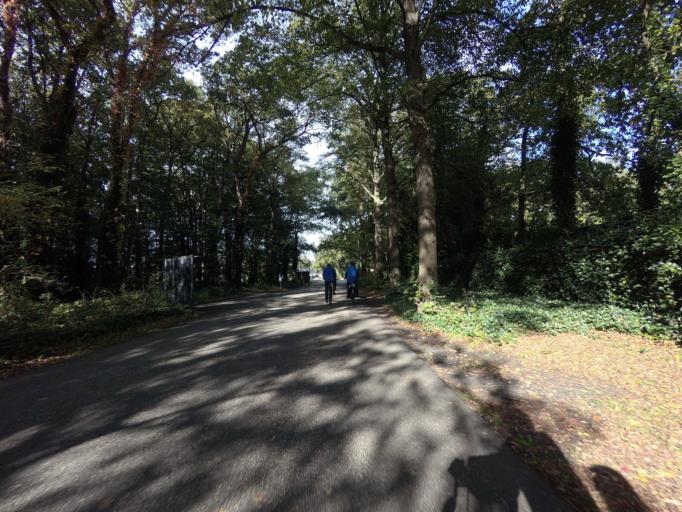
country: NL
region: North Holland
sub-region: Gemeente Wijdemeren
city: Nieuw-Loosdrecht
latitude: 52.2083
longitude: 5.1460
